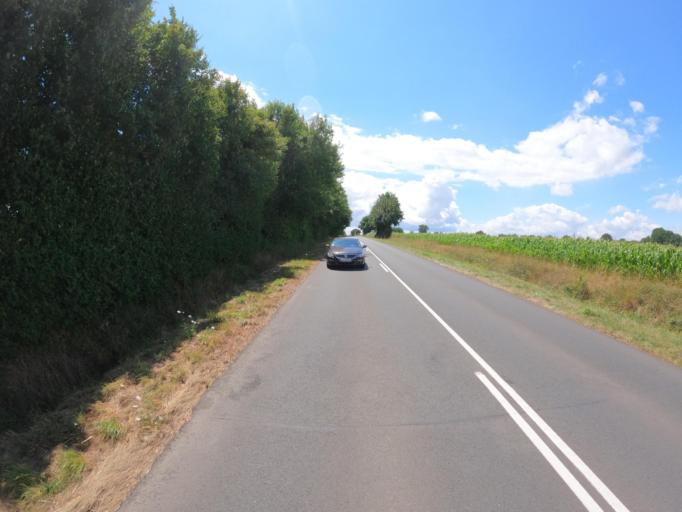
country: FR
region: Pays de la Loire
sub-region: Departement de Maine-et-Loire
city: Champigne
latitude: 47.6521
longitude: -0.5758
